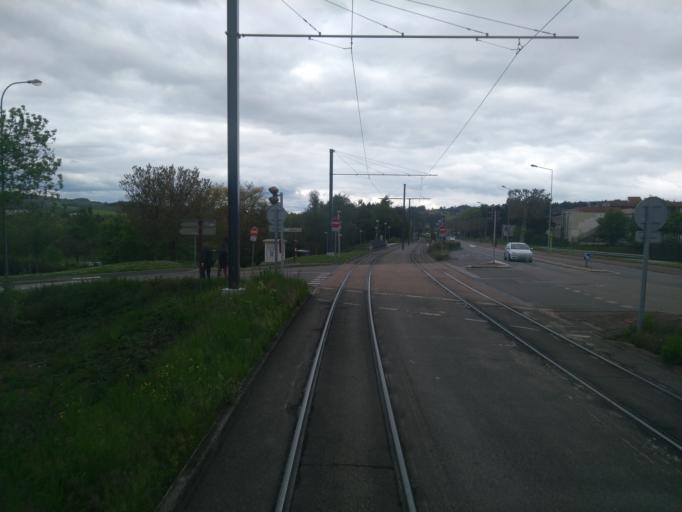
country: FR
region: Rhone-Alpes
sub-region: Departement de la Loire
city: Saint-Priest-en-Jarez
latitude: 45.4740
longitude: 4.3680
